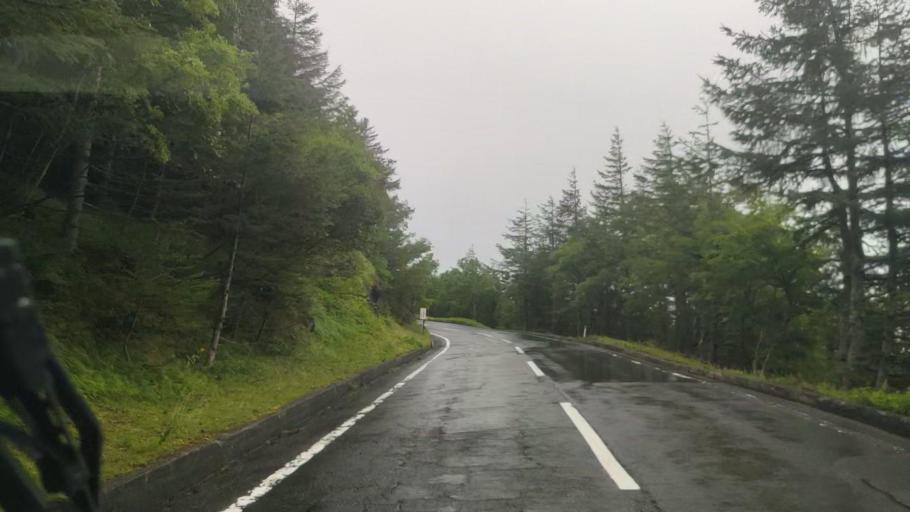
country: JP
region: Yamanashi
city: Fujikawaguchiko
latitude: 35.3348
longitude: 138.7316
